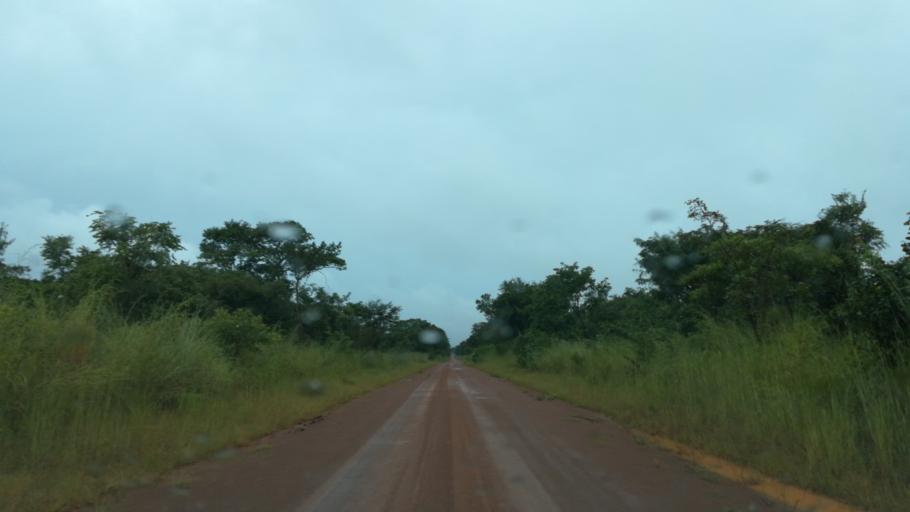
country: ZM
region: Luapula
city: Mwense
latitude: -10.7390
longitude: 28.2476
